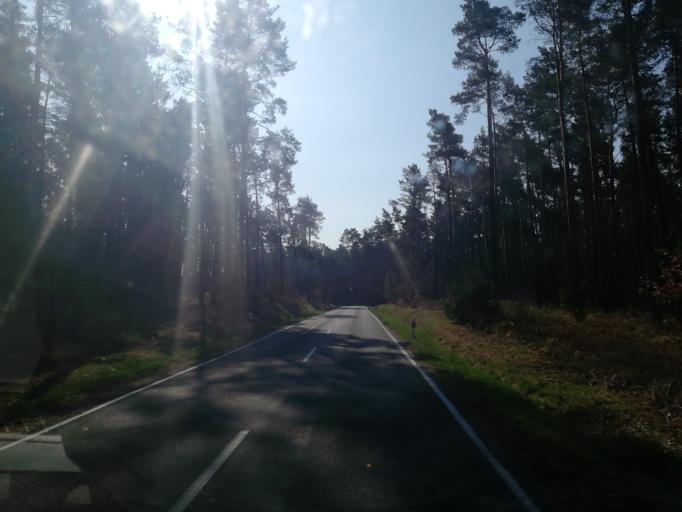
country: DE
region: Brandenburg
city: Sonnewalde
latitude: 51.7613
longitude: 13.6622
